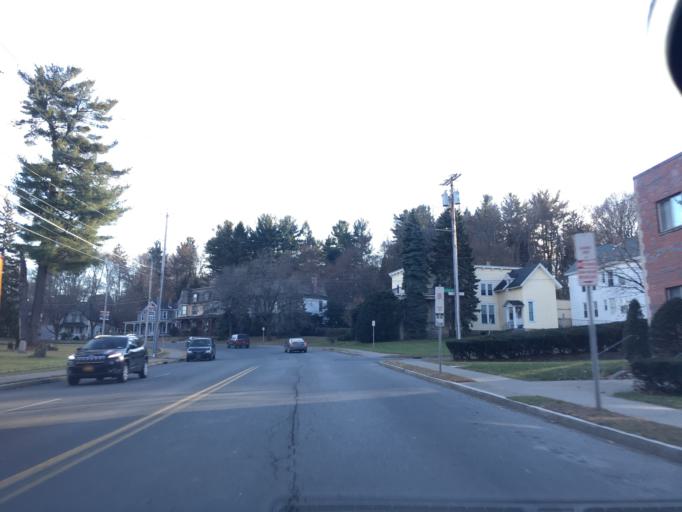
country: US
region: New York
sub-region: Rensselaer County
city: Troy
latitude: 42.7201
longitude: -73.6750
